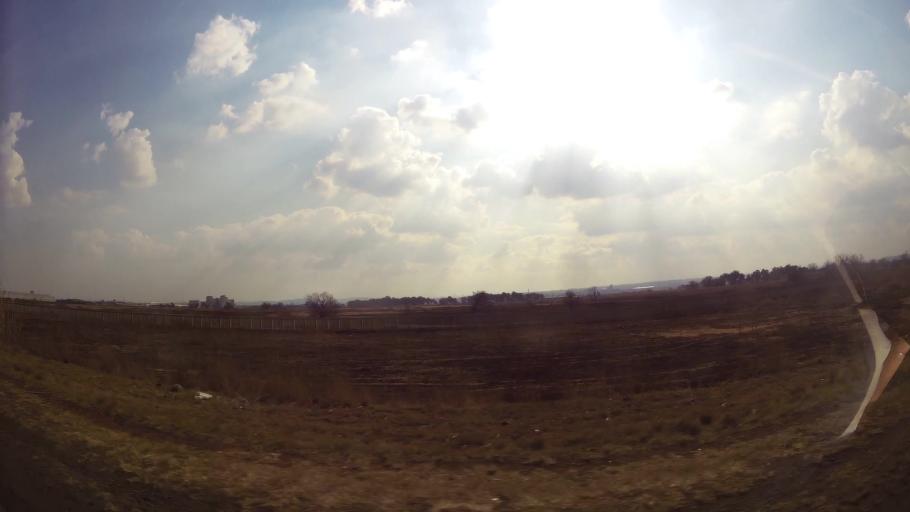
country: ZA
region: Gauteng
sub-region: Ekurhuleni Metropolitan Municipality
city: Germiston
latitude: -26.3017
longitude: 28.2120
